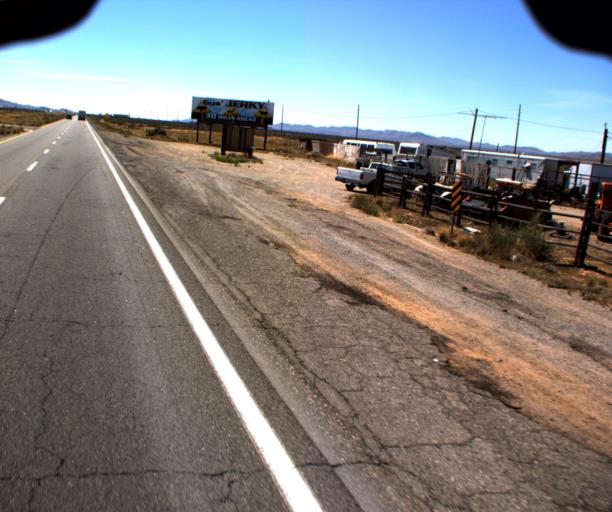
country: US
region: Arizona
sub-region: Mohave County
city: Dolan Springs
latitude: 35.5589
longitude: -114.3730
